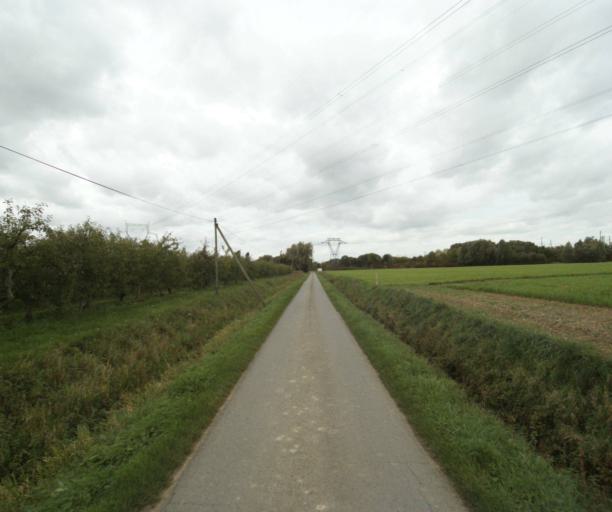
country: FR
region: Nord-Pas-de-Calais
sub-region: Departement du Nord
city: Erquinghem-Lys
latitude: 50.6695
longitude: 2.8266
